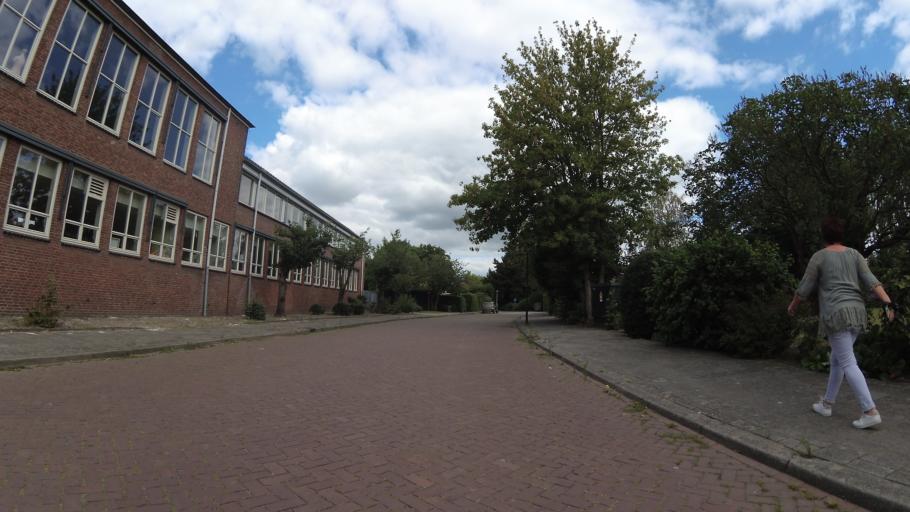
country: NL
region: North Brabant
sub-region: Gemeente Dongen
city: Dongen
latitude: 51.6313
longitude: 4.9399
